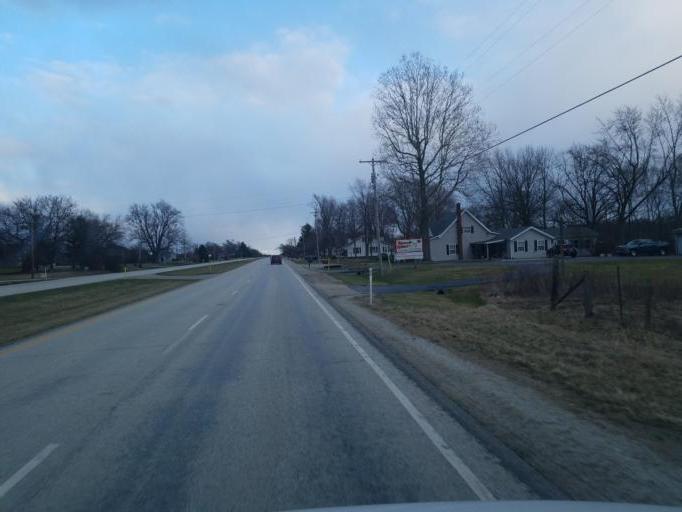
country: US
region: Indiana
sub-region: Hancock County
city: Greenfield
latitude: 39.7879
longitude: -85.7053
